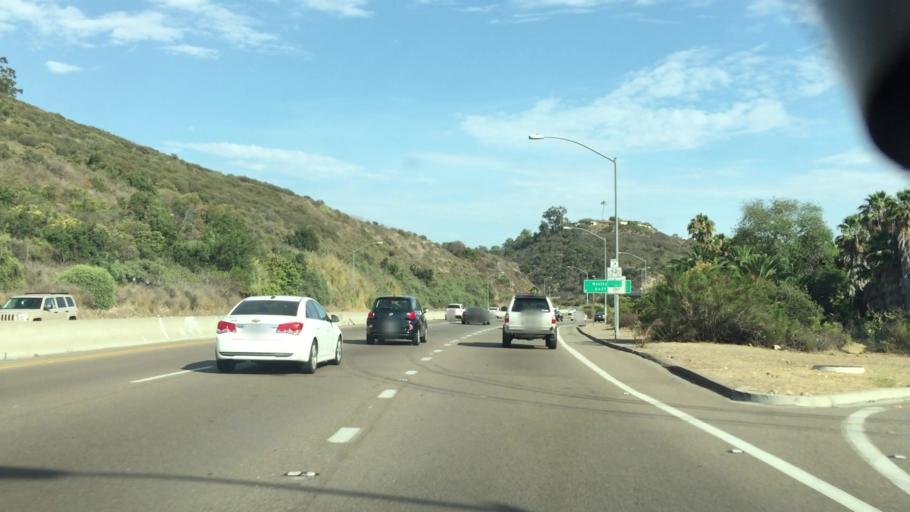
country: US
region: California
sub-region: San Diego County
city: Lemon Grove
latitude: 32.7758
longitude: -117.0992
